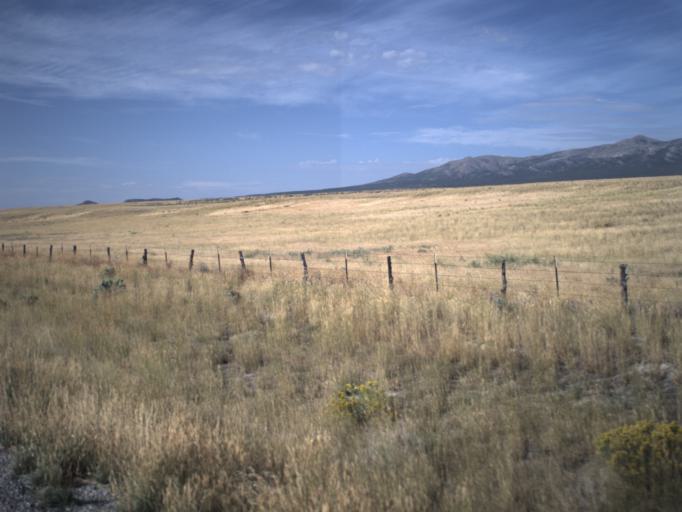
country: US
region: Idaho
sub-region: Oneida County
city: Malad City
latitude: 41.9210
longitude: -113.0951
